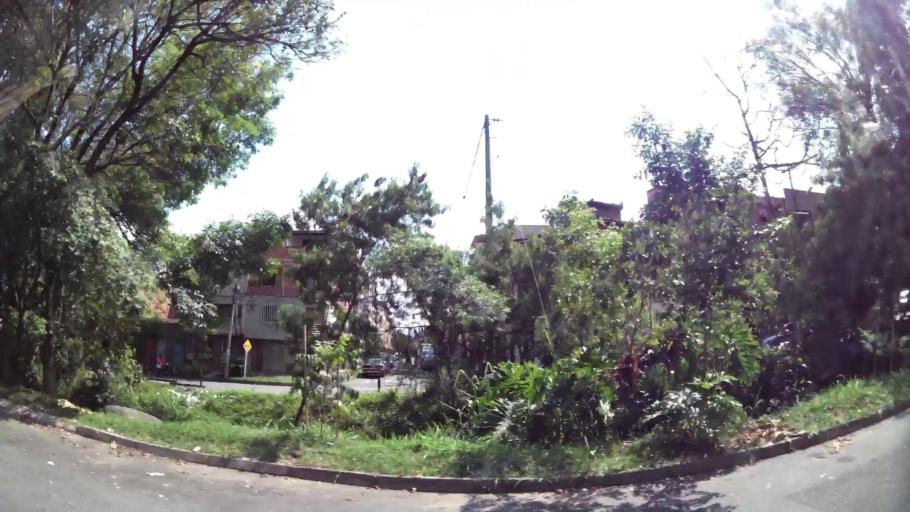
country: CO
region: Antioquia
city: Medellin
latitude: 6.2288
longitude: -75.5949
